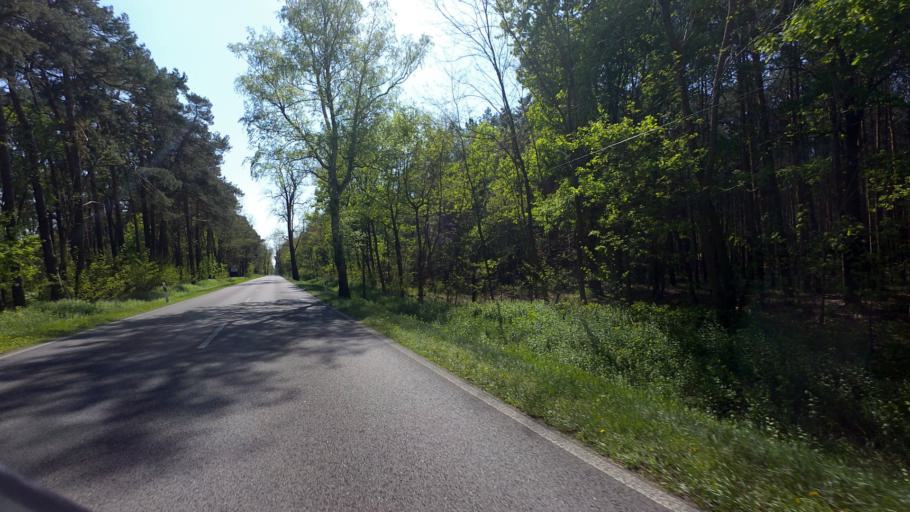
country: DE
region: Brandenburg
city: Tauche
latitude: 52.1333
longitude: 14.2009
